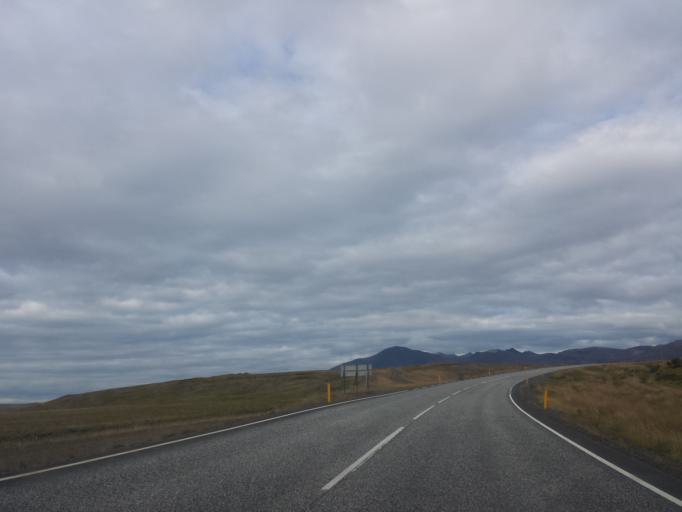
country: IS
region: West
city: Borgarnes
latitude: 64.3789
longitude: -21.8516
